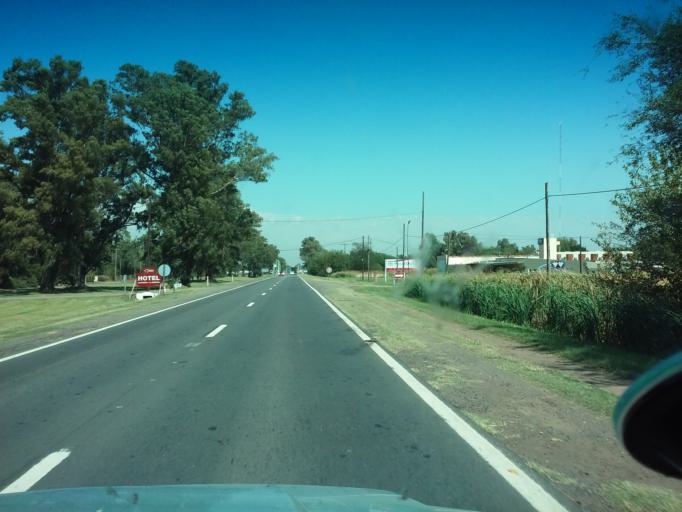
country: AR
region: Buenos Aires
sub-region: Partido de Nueve de Julio
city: Nueve de Julio
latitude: -35.4859
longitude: -60.8842
